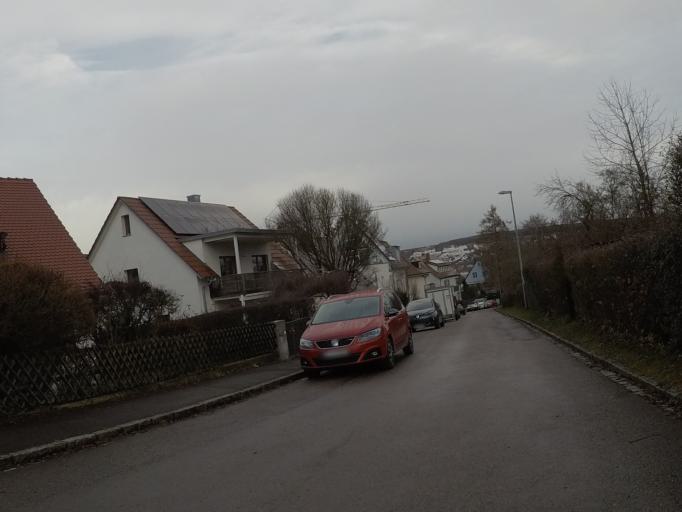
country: DE
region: Baden-Wuerttemberg
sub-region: Tuebingen Region
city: Ulm
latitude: 48.3904
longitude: 9.9521
